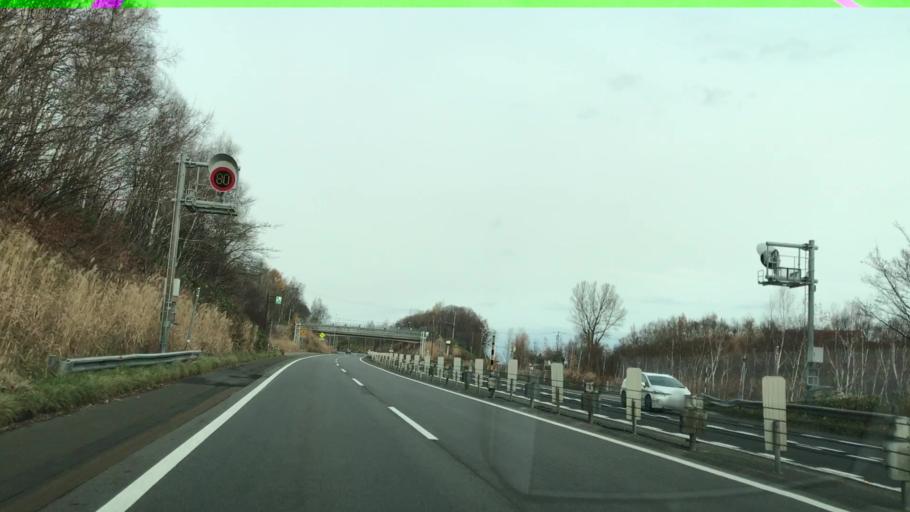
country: JP
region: Hokkaido
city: Otaru
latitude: 43.1576
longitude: 141.1103
